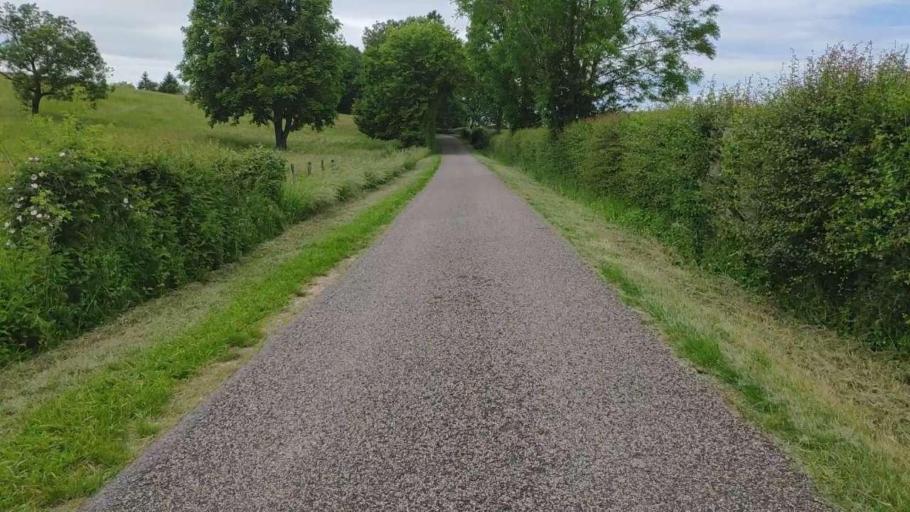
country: FR
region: Franche-Comte
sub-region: Departement du Jura
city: Perrigny
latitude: 46.7591
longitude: 5.5654
